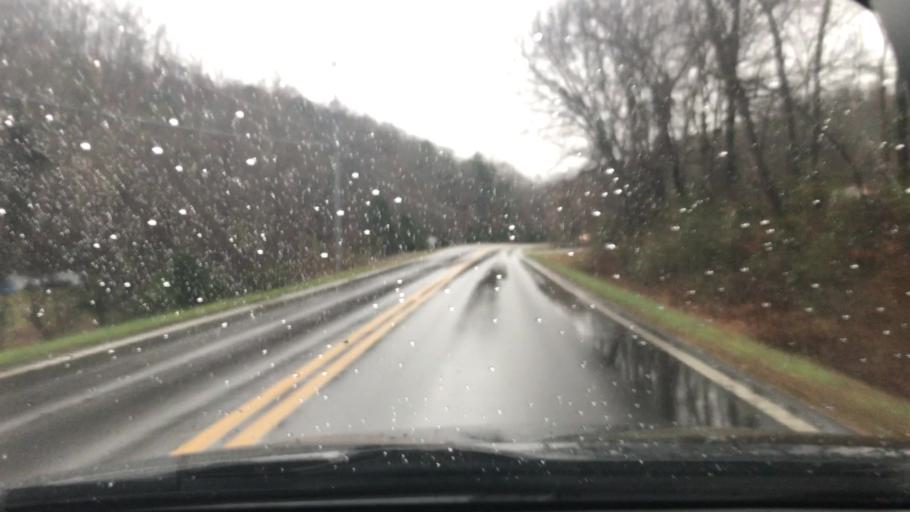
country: US
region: Tennessee
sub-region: Cheatham County
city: Ashland City
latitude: 36.2774
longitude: -87.1381
